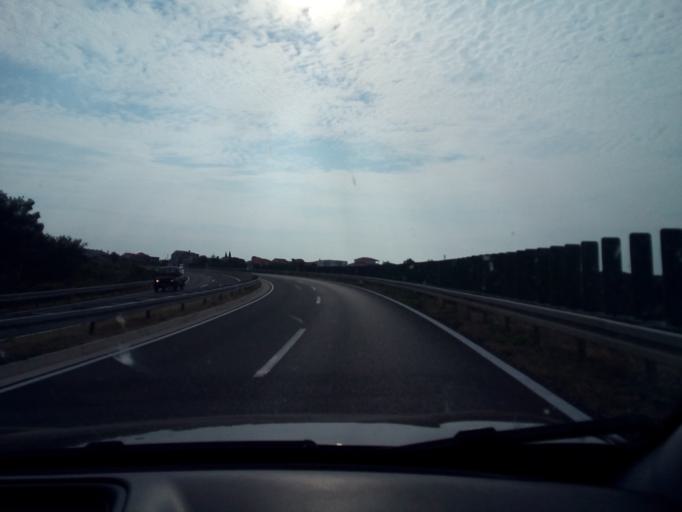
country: HR
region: Zadarska
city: Bibinje
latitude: 44.0951
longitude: 15.2811
